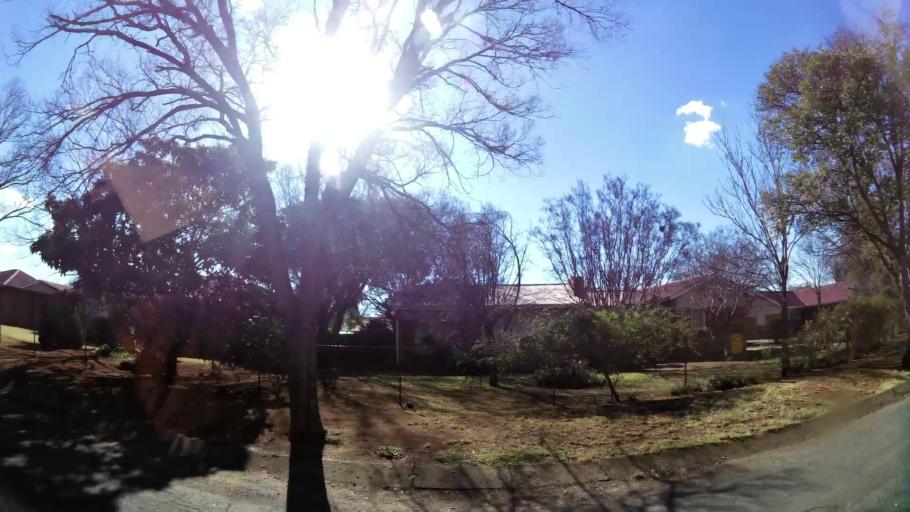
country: ZA
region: Gauteng
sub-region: West Rand District Municipality
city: Carletonville
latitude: -26.3615
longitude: 27.3643
